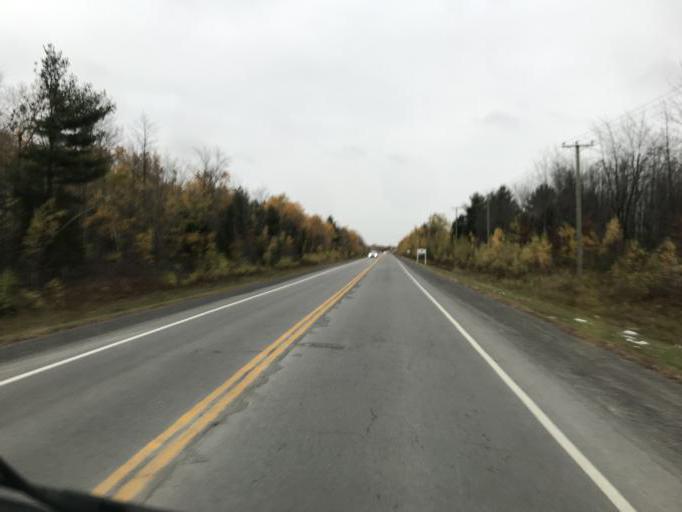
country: CA
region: Quebec
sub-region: Lanaudiere
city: Lorraine
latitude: 45.6862
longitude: -73.7773
